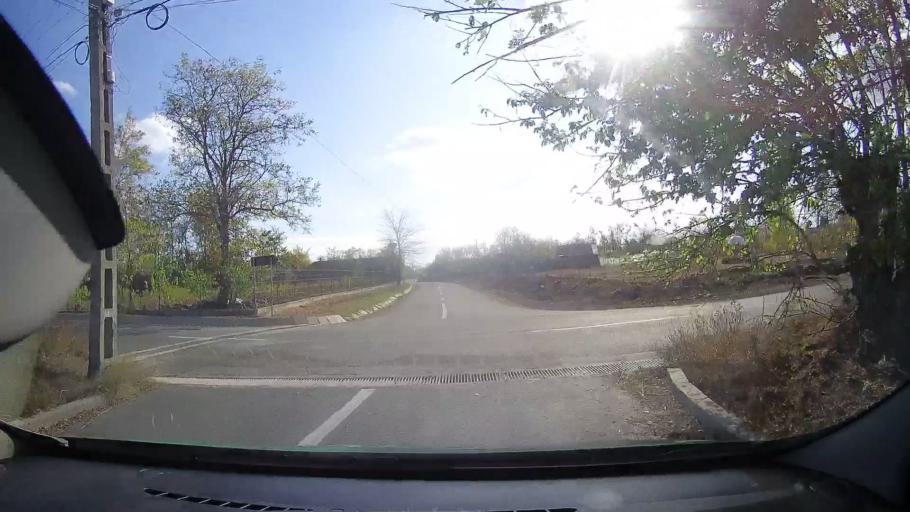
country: RO
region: Constanta
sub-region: Comuna Istria
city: Istria
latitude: 44.5763
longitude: 28.7128
